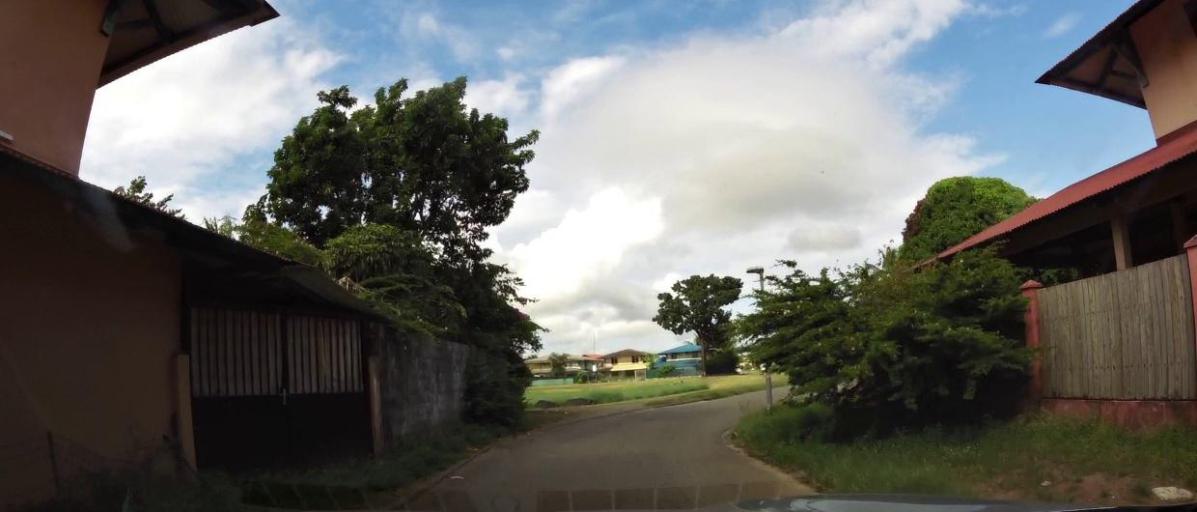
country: GF
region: Guyane
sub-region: Guyane
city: Kourou
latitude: 5.1681
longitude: -52.6524
